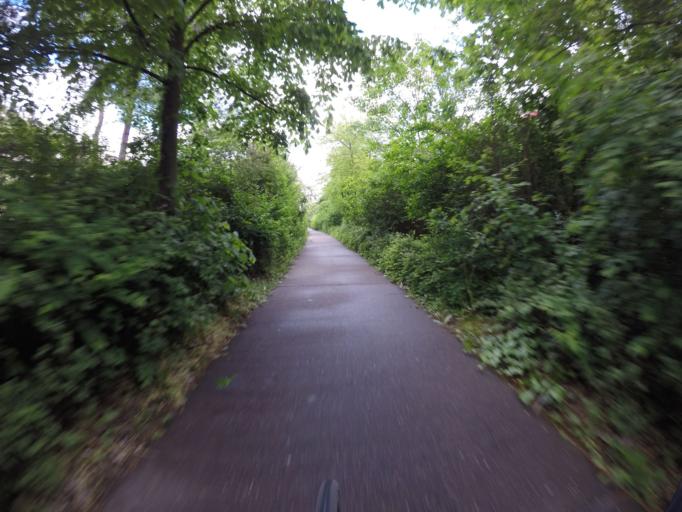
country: DE
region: Berlin
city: Marzahn
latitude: 52.5564
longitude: 13.5679
